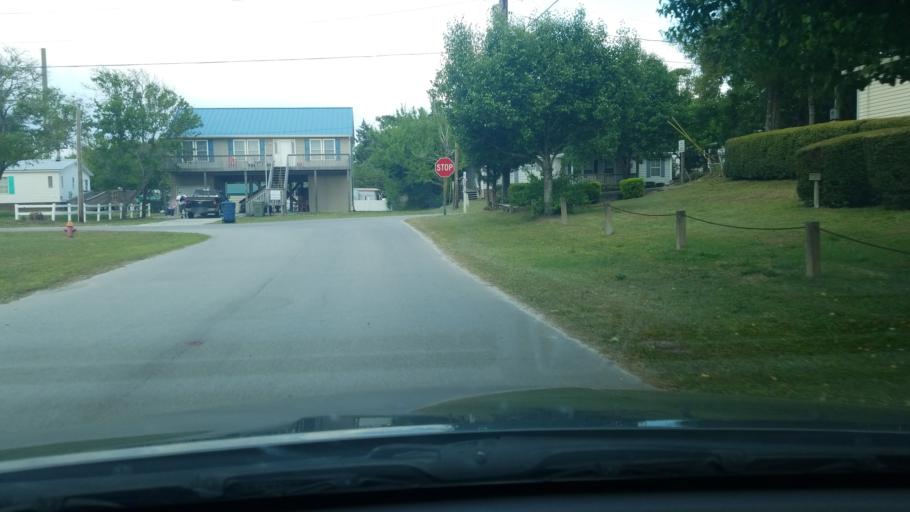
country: US
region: North Carolina
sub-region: Carteret County
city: Cape Carteret
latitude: 34.6633
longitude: -77.0385
